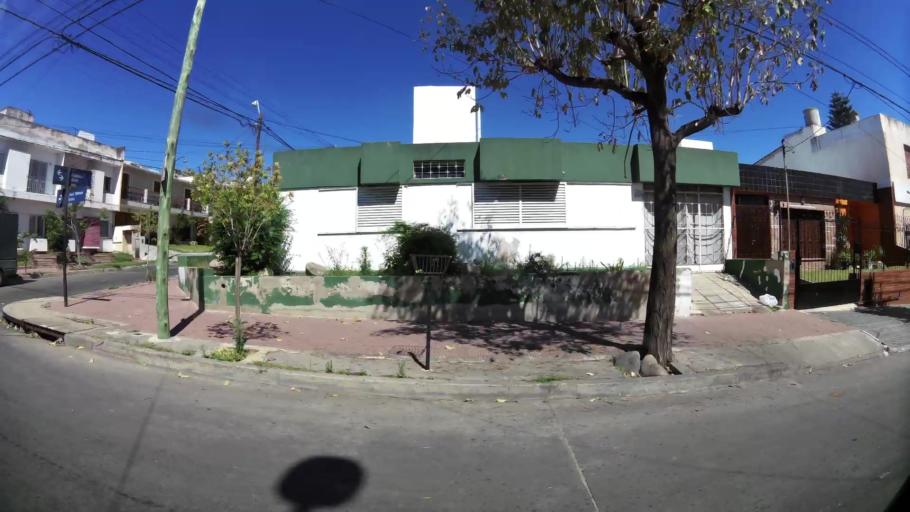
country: AR
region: Cordoba
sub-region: Departamento de Capital
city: Cordoba
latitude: -31.4273
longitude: -64.1588
